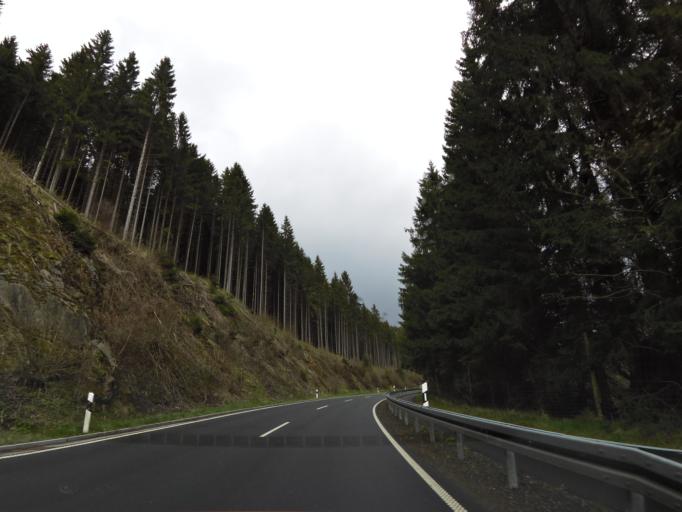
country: DE
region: Lower Saxony
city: Schulenberg im Oberharz
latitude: 51.8197
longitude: 10.4388
